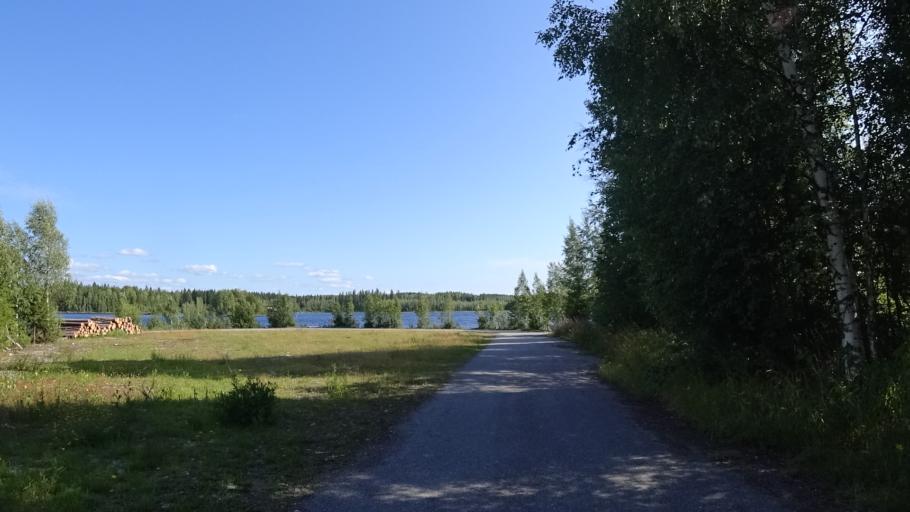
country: FI
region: North Karelia
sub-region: Joensuu
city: Eno
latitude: 62.8011
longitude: 30.1196
